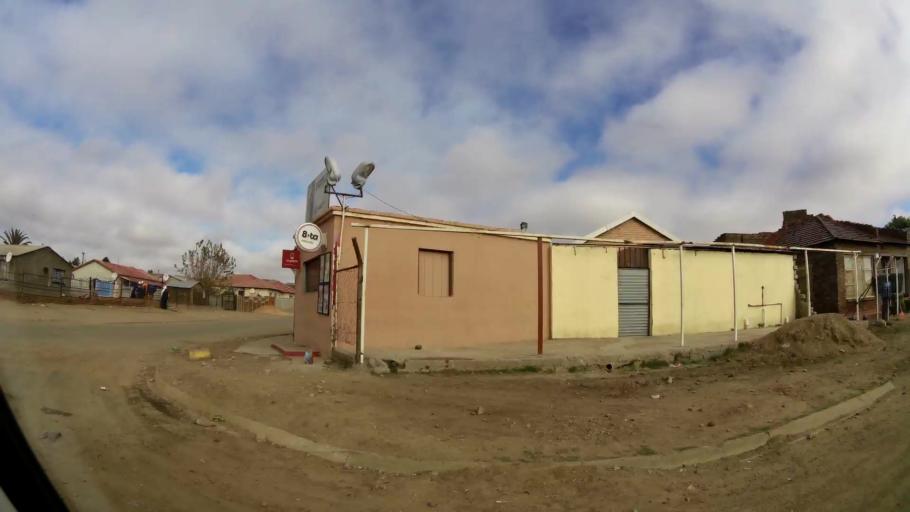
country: ZA
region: Limpopo
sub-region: Capricorn District Municipality
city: Polokwane
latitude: -23.8524
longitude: 29.3872
